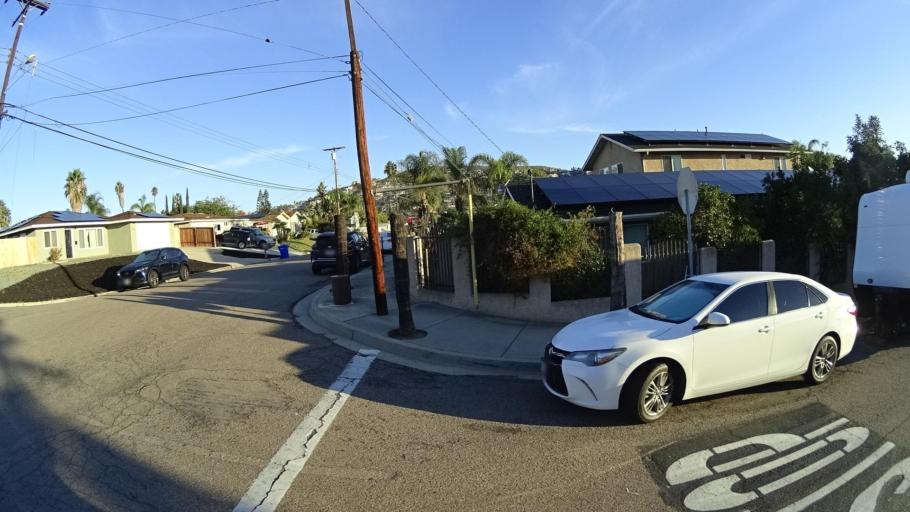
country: US
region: California
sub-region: San Diego County
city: La Presa
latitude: 32.7097
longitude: -116.9930
